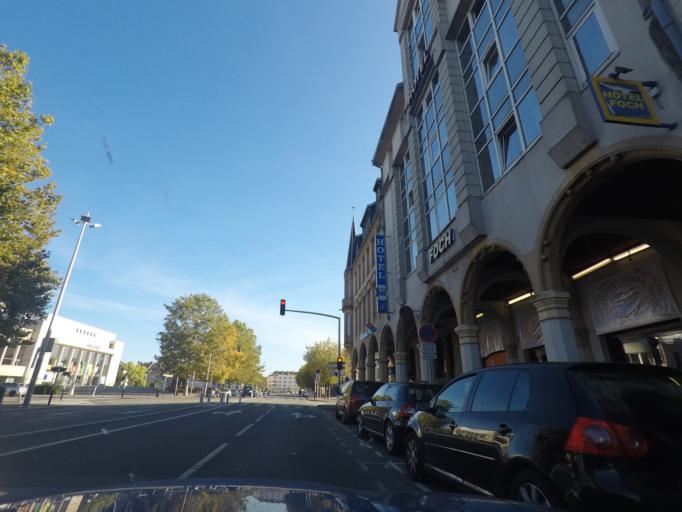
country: FR
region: Lorraine
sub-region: Departement de la Moselle
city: Thionville
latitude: 49.3599
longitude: 6.1632
